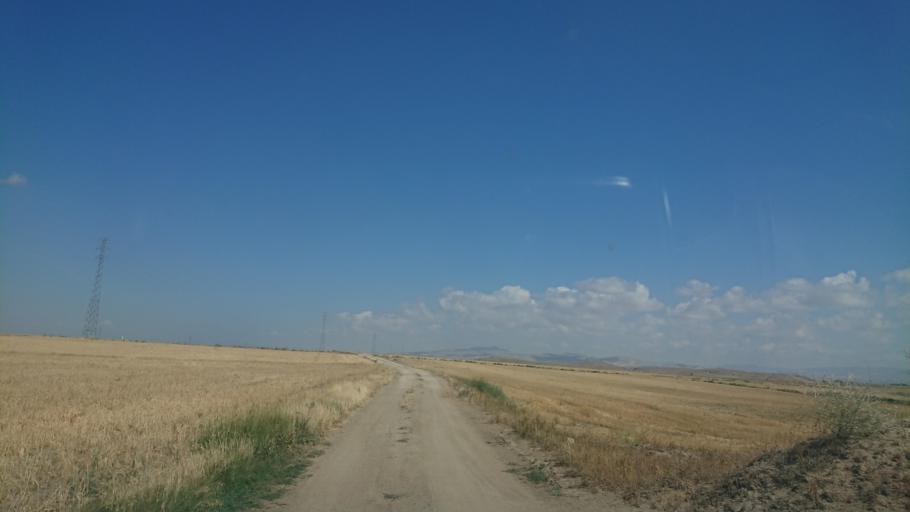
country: TR
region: Aksaray
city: Sariyahsi
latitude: 38.9986
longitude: 33.8929
